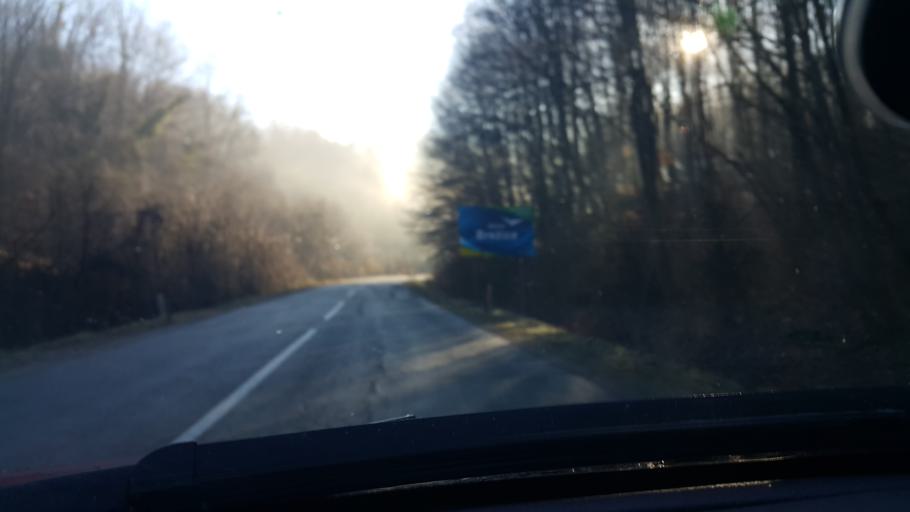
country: SI
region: Bistrica ob Sotli
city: Bistrica ob Sotli
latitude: 46.0441
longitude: 15.6845
